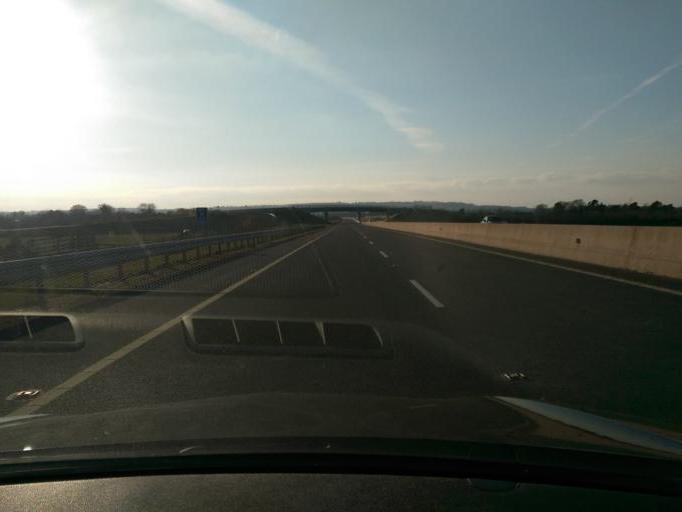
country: IE
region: Munster
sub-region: North Tipperary
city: Roscrea
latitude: 52.9251
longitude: -7.7452
